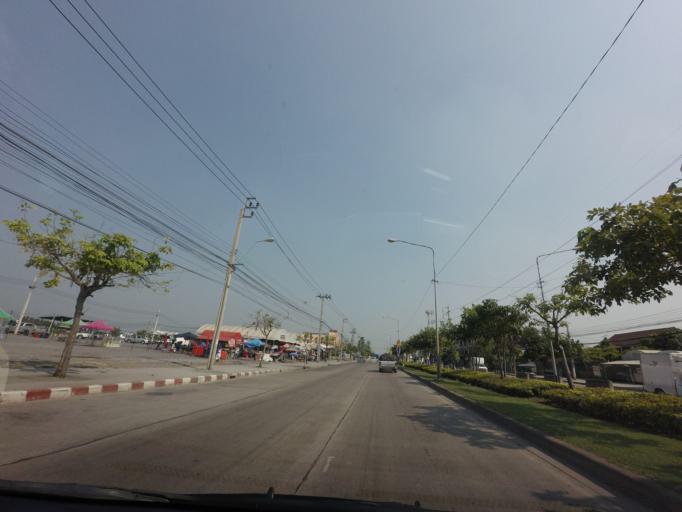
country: TH
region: Bangkok
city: Lat Krabang
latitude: 13.7529
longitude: 100.7748
